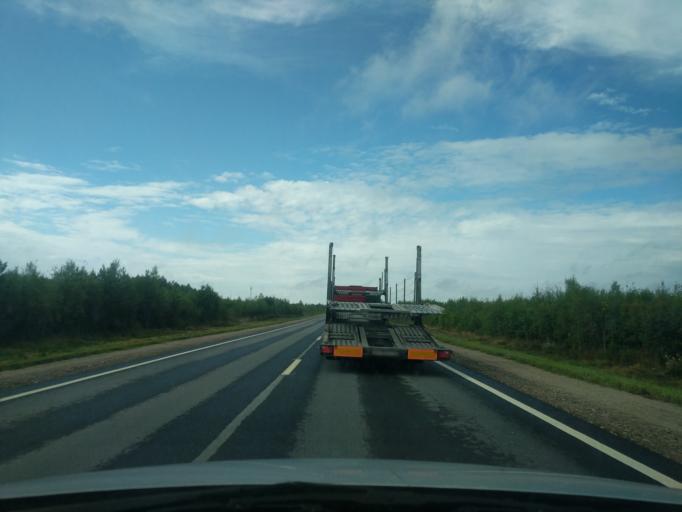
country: RU
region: Kostroma
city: Sudislavl'
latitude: 57.8212
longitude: 41.9109
